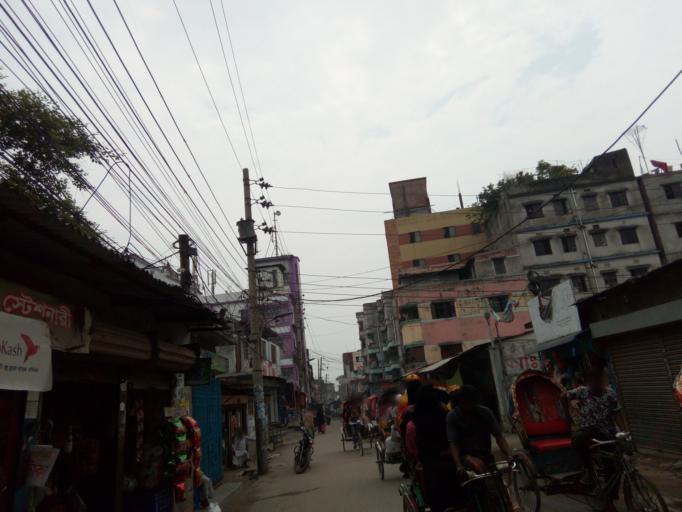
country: BD
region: Dhaka
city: Azimpur
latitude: 23.7094
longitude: 90.3685
